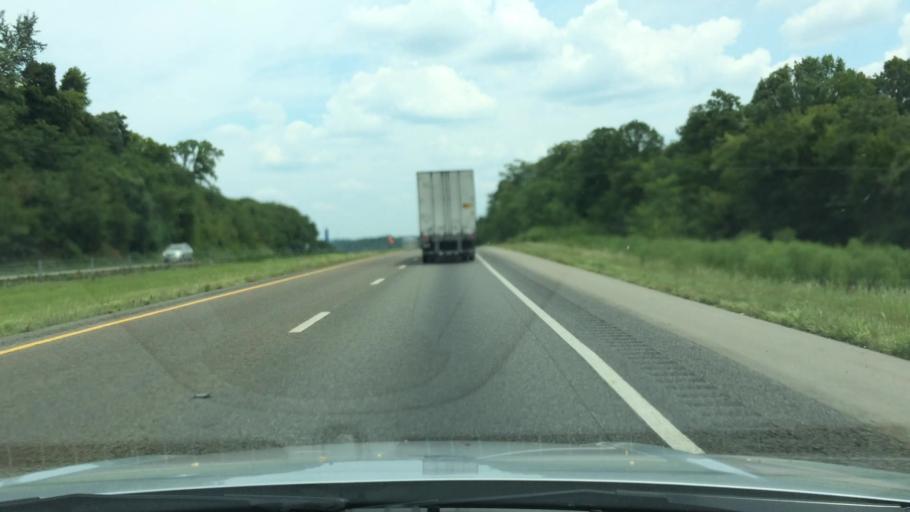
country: US
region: Tennessee
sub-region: Maury County
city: Spring Hill
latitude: 35.6345
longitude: -86.8950
